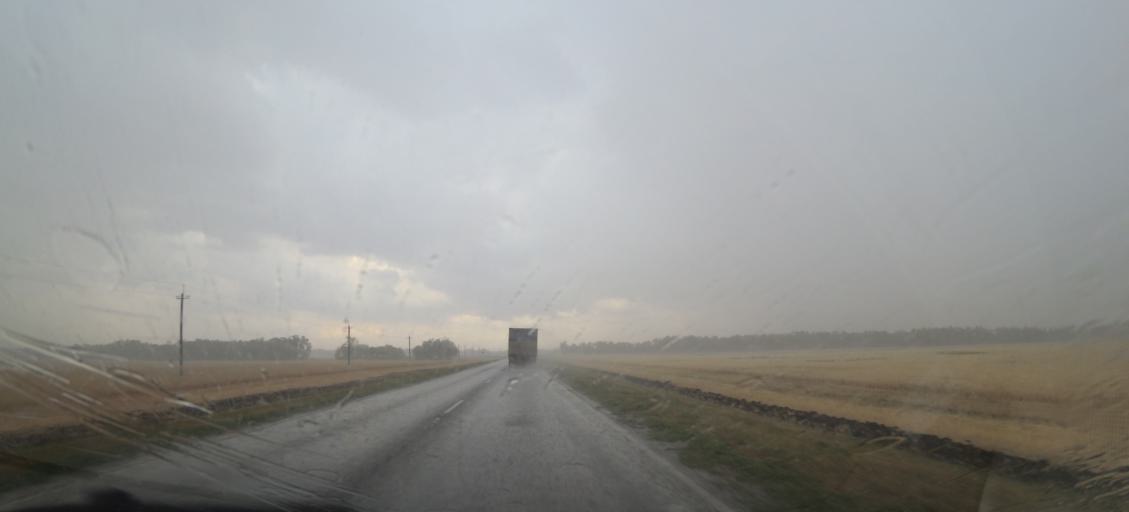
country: RU
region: Rostov
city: Gundorovskiy
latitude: 46.8540
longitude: 41.9267
